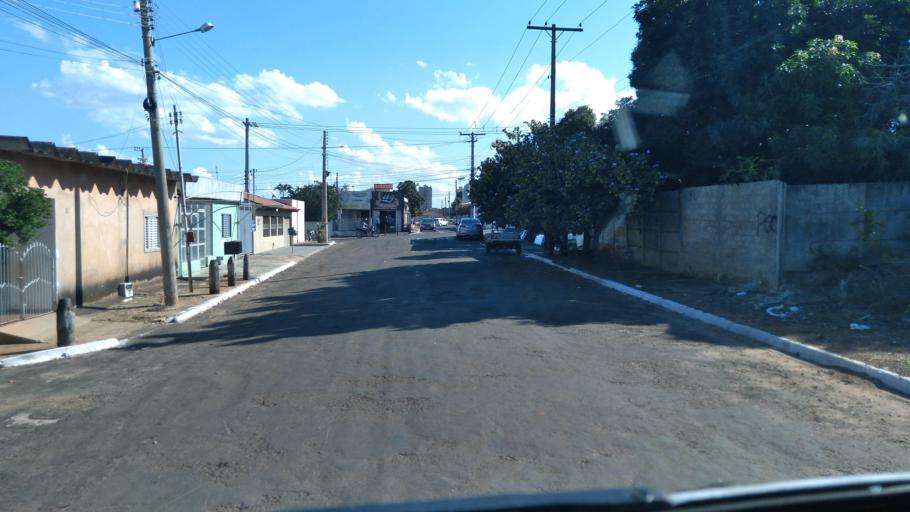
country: BR
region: Goias
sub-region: Mineiros
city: Mineiros
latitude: -17.5608
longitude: -52.5491
